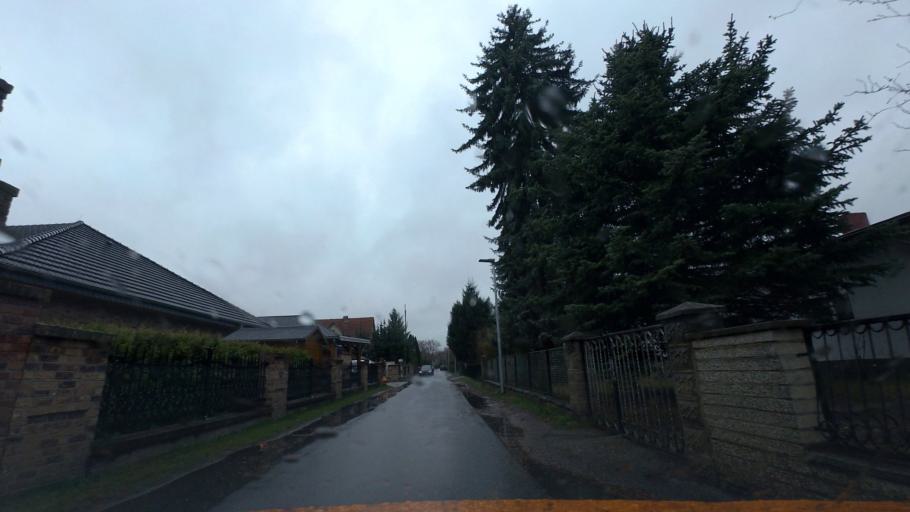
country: DE
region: Brandenburg
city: Brieselang
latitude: 52.5862
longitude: 13.0020
